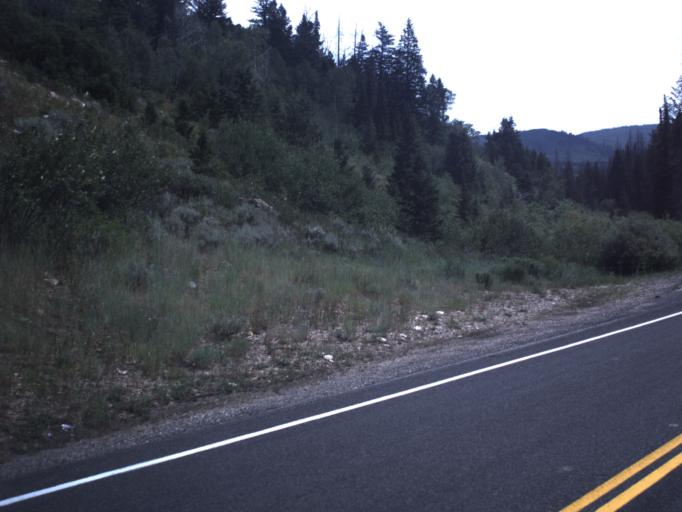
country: US
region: Utah
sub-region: Summit County
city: Francis
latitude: 40.5170
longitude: -111.0775
